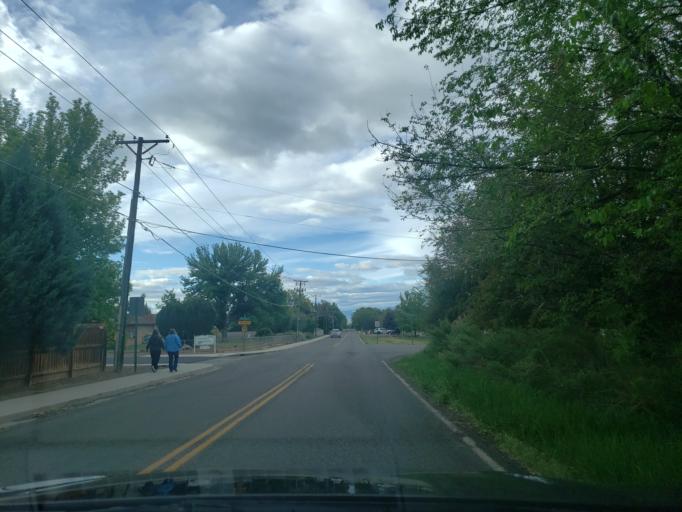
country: US
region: Colorado
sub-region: Mesa County
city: Redlands
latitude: 39.0972
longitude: -108.6687
